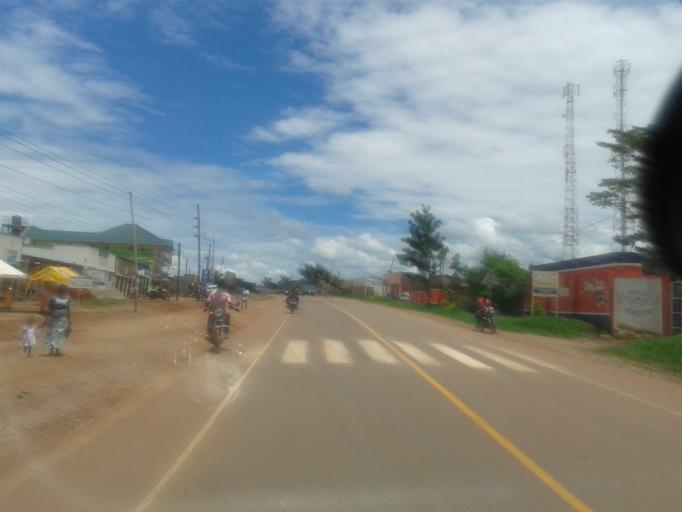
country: UG
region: Western Region
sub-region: Kiryandongo District
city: Kiryandongo
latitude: 1.8082
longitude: 32.0108
